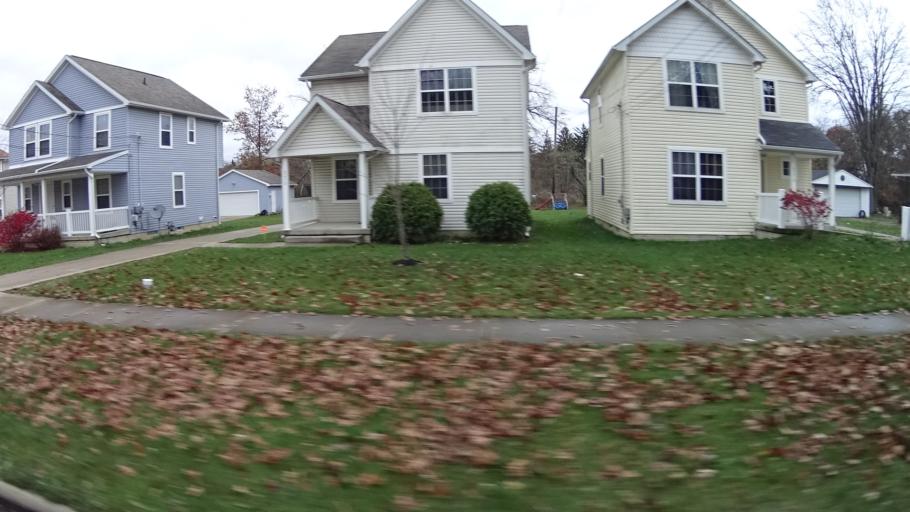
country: US
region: Ohio
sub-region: Lorain County
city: Elyria
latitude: 41.3614
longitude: -82.1161
